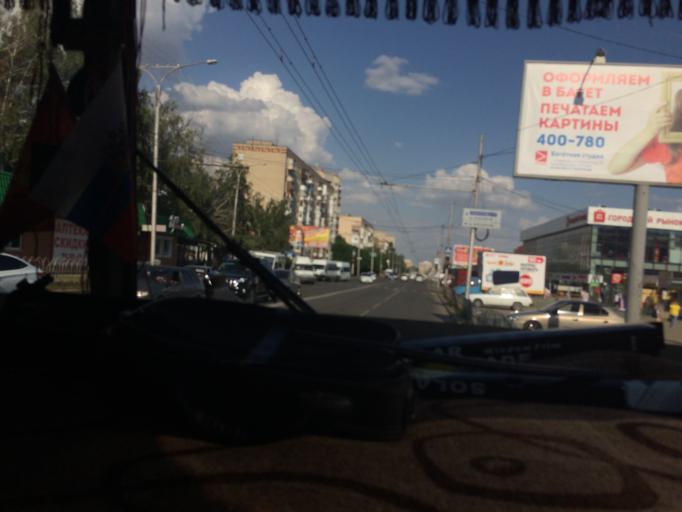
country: RU
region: Stavropol'skiy
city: Stavropol'
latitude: 45.0141
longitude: 41.9166
